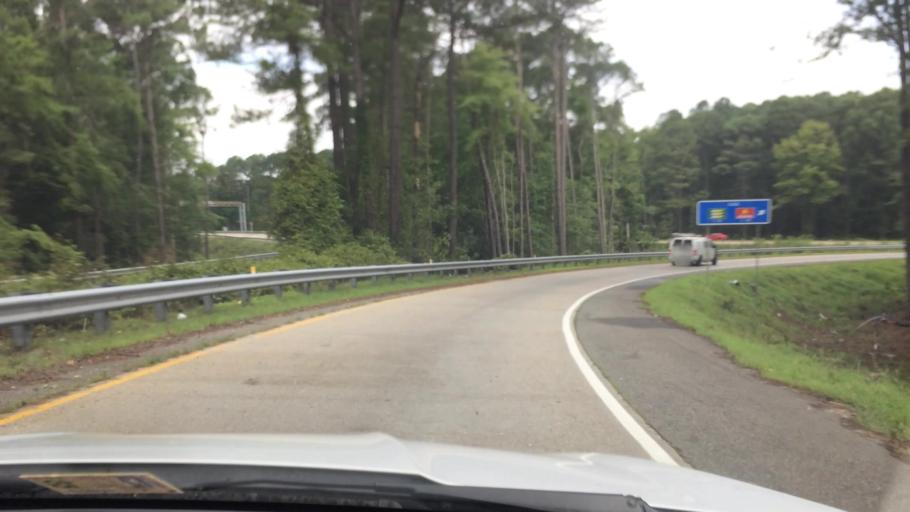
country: US
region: Virginia
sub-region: York County
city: Yorktown
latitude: 37.1731
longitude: -76.5528
